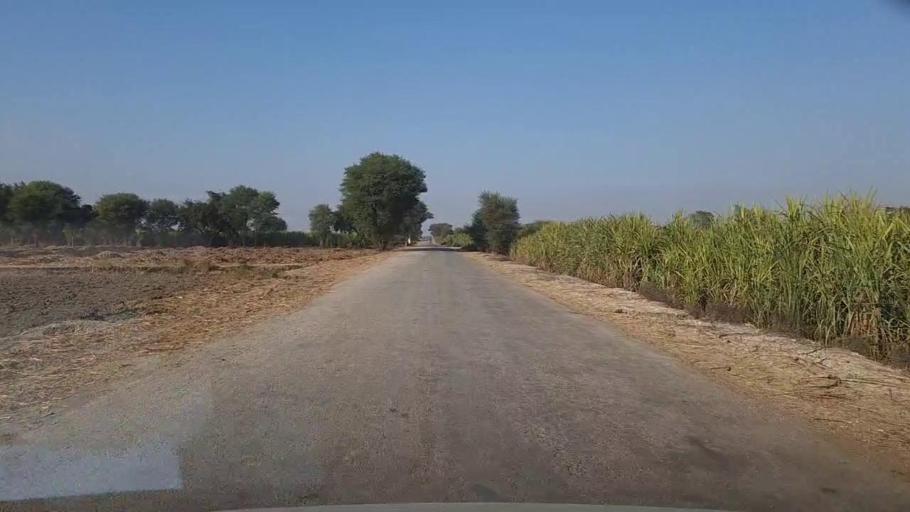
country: PK
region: Sindh
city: Dadu
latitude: 26.8488
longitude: 67.7937
